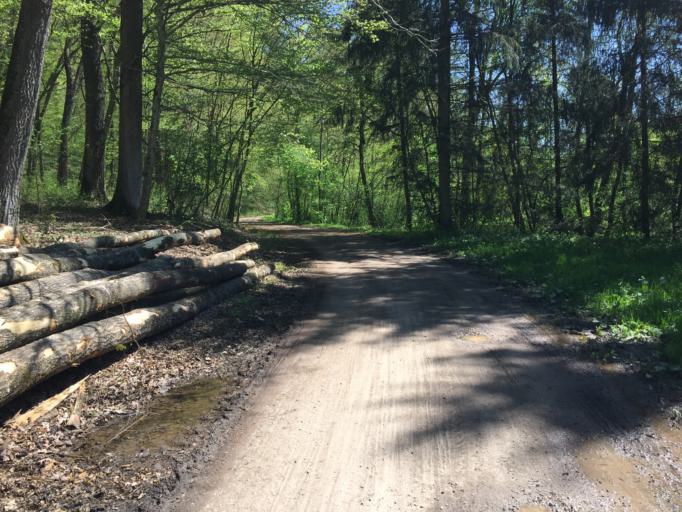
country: DE
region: Baden-Wuerttemberg
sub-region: Tuebingen Region
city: Gomaringen
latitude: 48.4767
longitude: 9.0869
